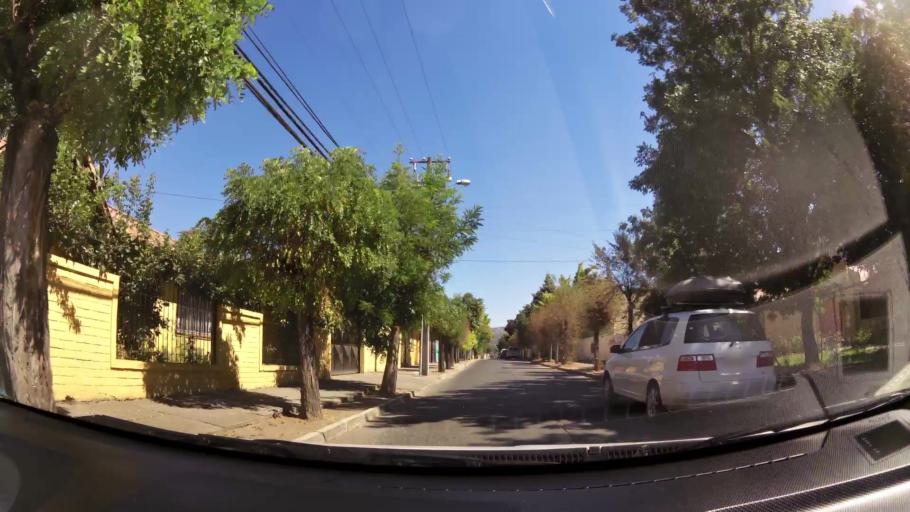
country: CL
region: O'Higgins
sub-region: Provincia de Colchagua
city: Chimbarongo
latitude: -34.5837
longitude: -70.9930
